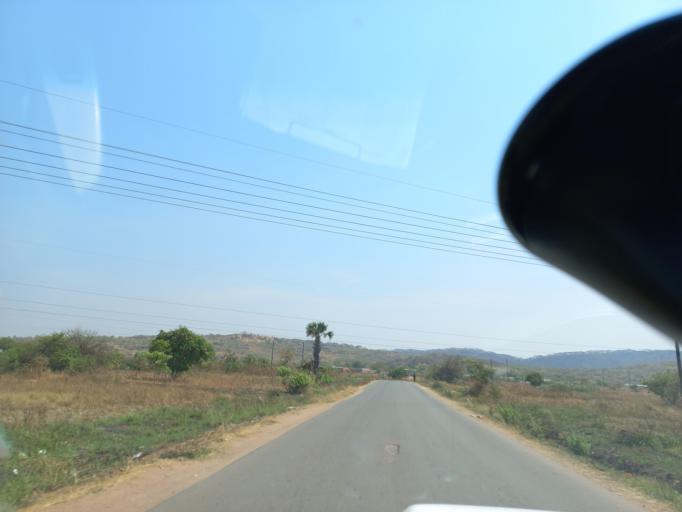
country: ZM
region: Lusaka
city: Kafue
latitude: -15.7417
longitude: 28.1739
